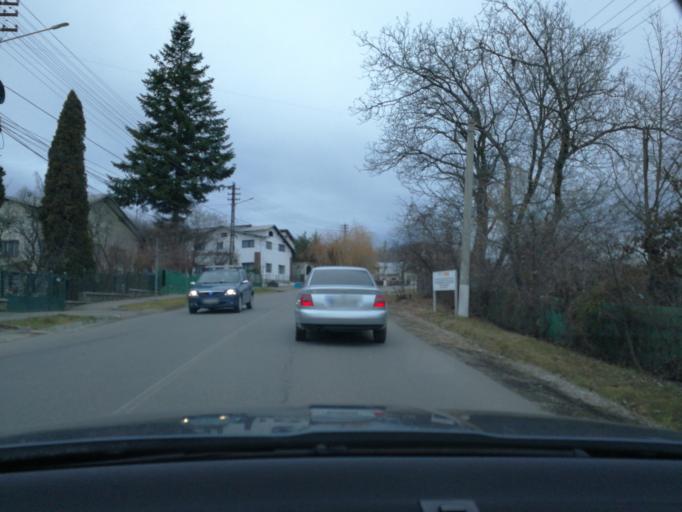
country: RO
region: Prahova
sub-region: Comuna Cornu
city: Cornu de Jos
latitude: 45.1498
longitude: 25.6892
